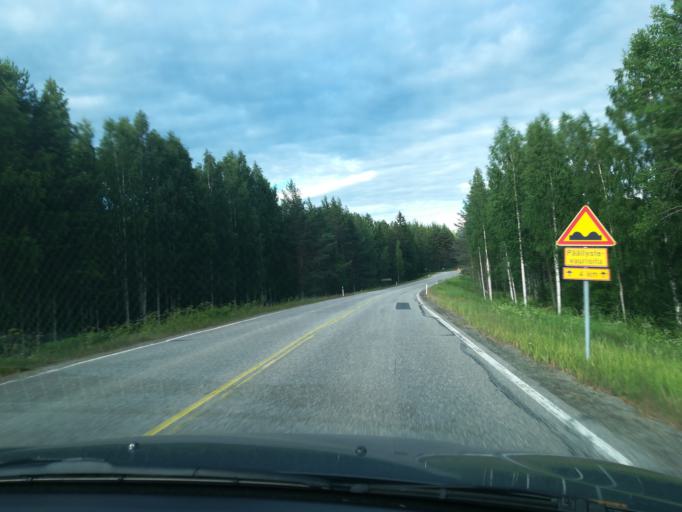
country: FI
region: South Karelia
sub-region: Lappeenranta
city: Savitaipale
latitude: 61.5389
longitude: 27.7047
